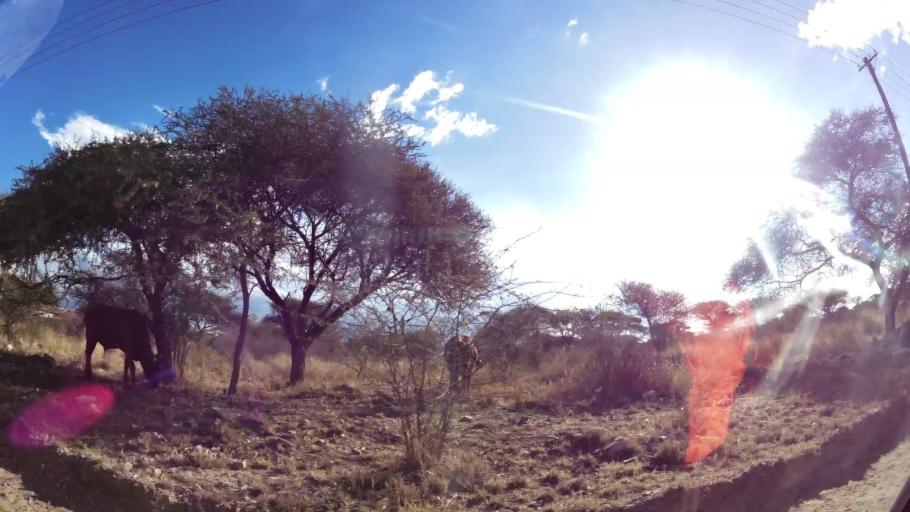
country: ZA
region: Limpopo
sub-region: Capricorn District Municipality
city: Polokwane
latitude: -23.9373
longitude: 29.4443
